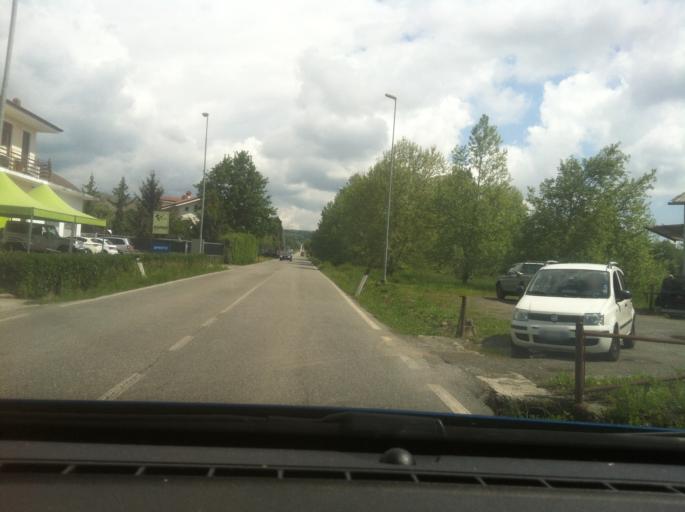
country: IT
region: Piedmont
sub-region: Provincia di Torino
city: Baldissero Canavese
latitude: 45.3932
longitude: 7.7322
